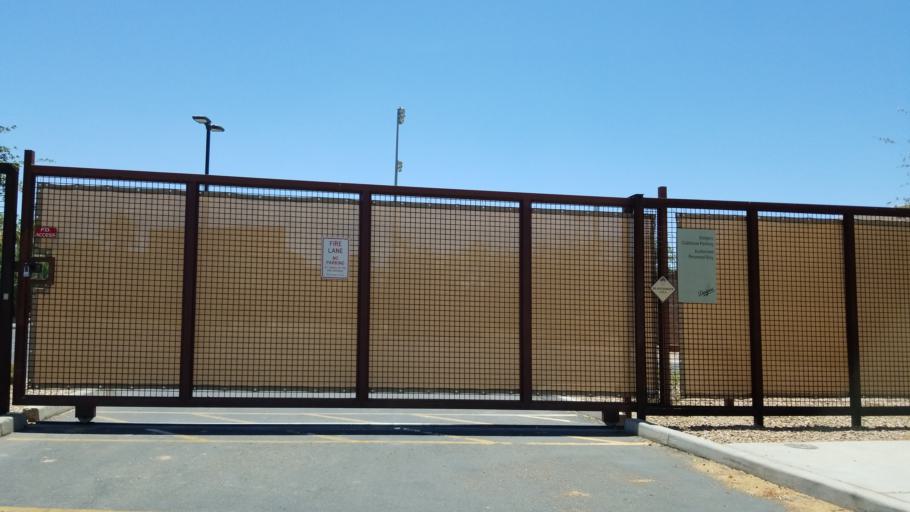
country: US
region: Arizona
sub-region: Maricopa County
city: Litchfield Park
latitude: 33.5151
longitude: -112.2947
